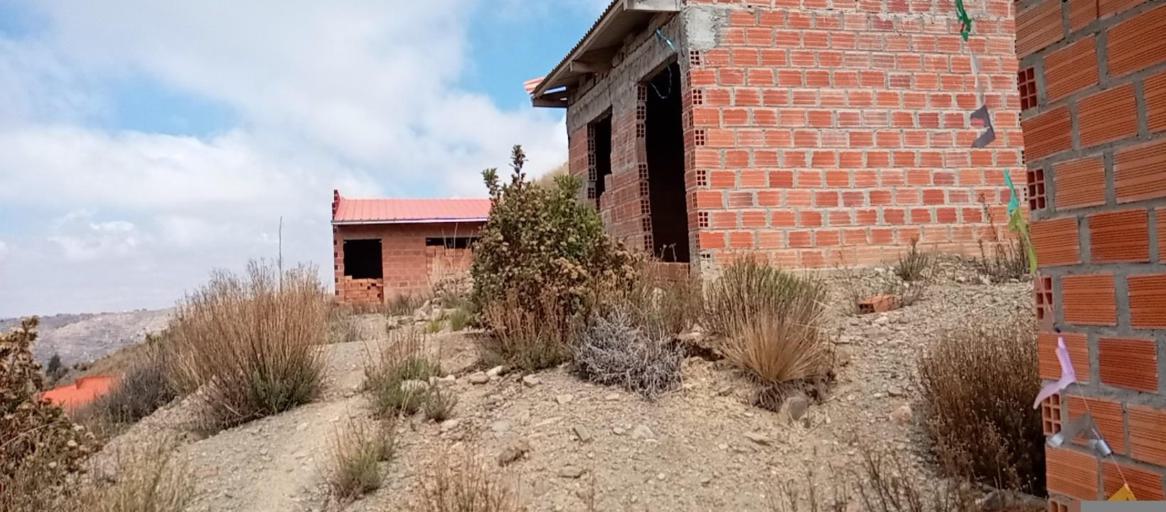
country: BO
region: La Paz
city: La Paz
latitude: -16.4655
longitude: -68.1390
